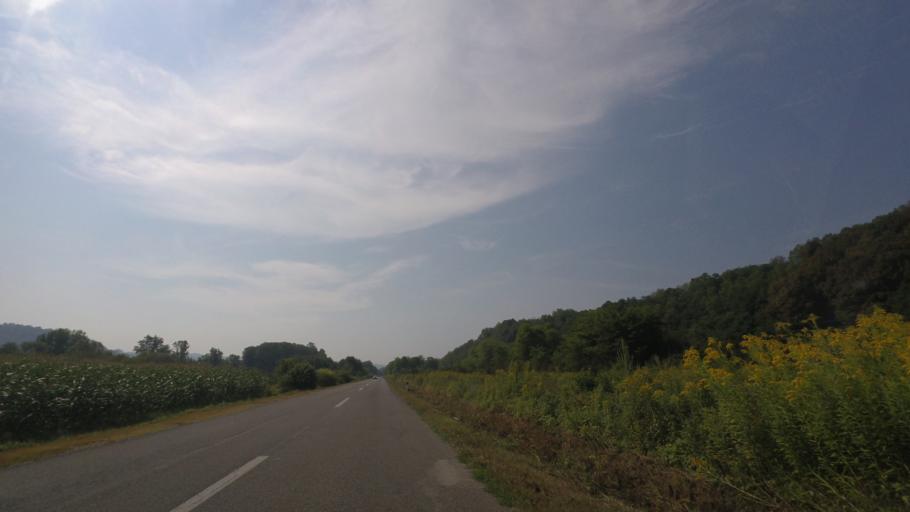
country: BA
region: Republika Srpska
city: Dobrljin
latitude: 45.1726
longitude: 16.4727
